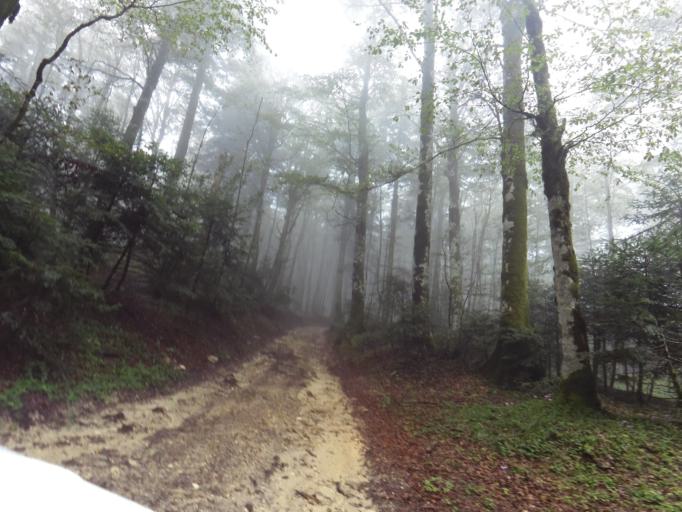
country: IT
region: Calabria
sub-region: Provincia di Vibo-Valentia
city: Mongiana
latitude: 38.5387
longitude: 16.3516
